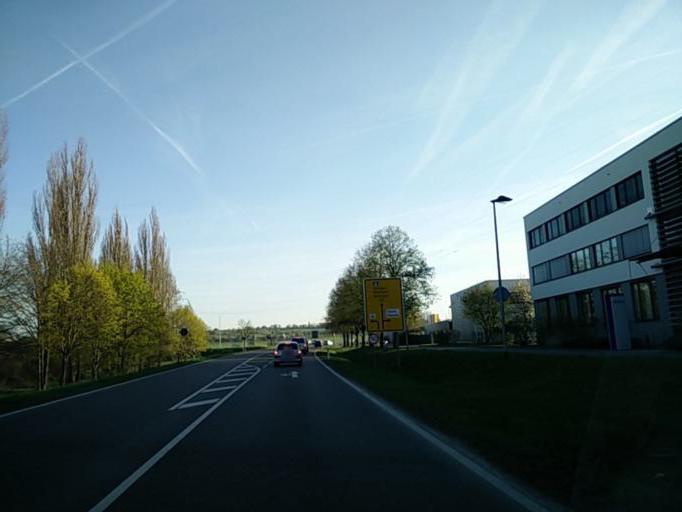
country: DE
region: Baden-Wuerttemberg
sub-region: Regierungsbezirk Stuttgart
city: Herrenberg
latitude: 48.6032
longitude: 8.8737
